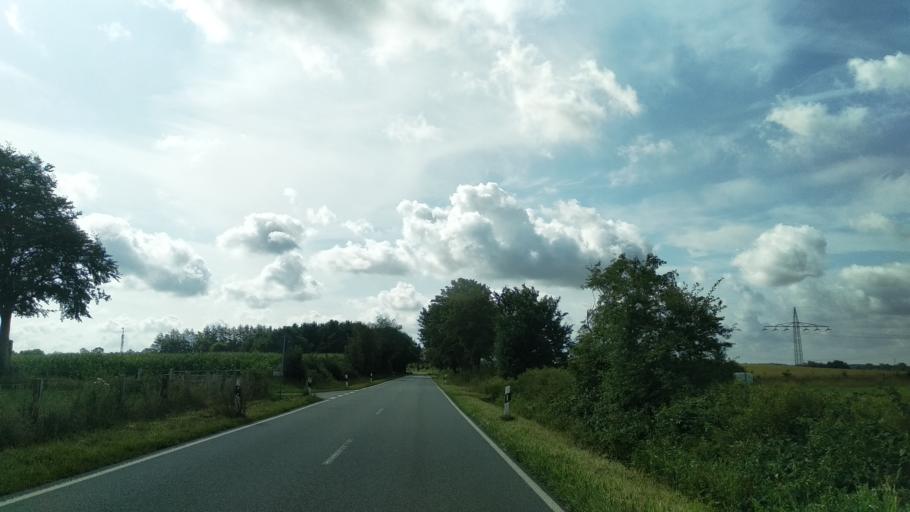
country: DE
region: Schleswig-Holstein
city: Geltorf
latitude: 54.4386
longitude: 9.6018
